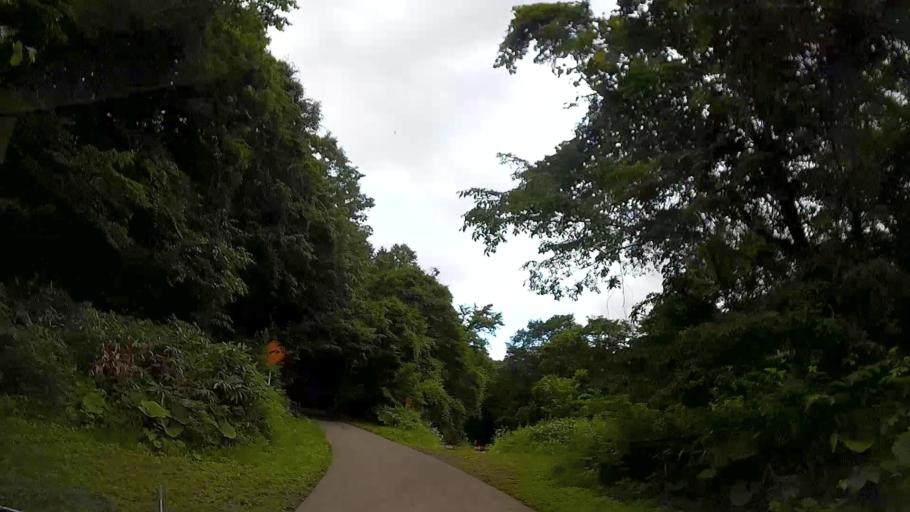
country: JP
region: Hokkaido
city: Nanae
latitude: 42.0424
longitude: 140.4865
